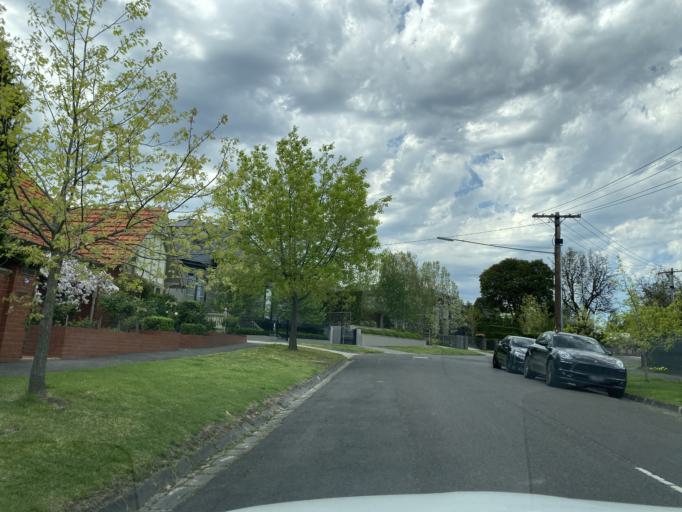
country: AU
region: Victoria
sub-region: Boroondara
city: Canterbury
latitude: -37.8274
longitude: 145.0759
